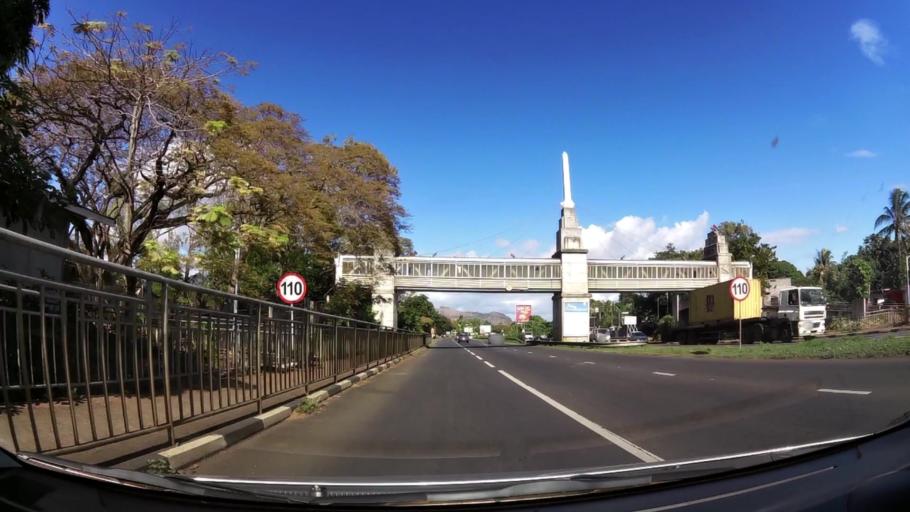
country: MU
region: Pamplemousses
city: Terre Rouge
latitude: -20.1271
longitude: 57.5315
